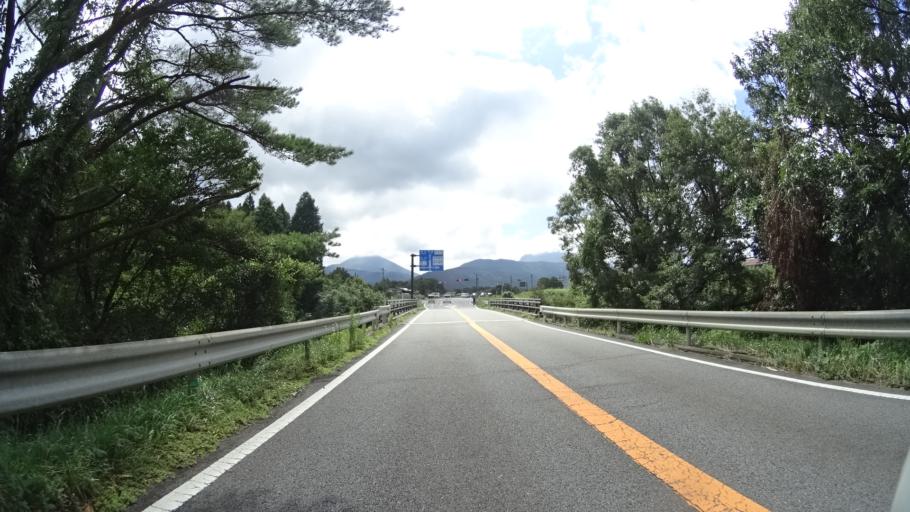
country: JP
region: Oita
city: Tsukawaki
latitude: 33.1583
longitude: 131.2406
